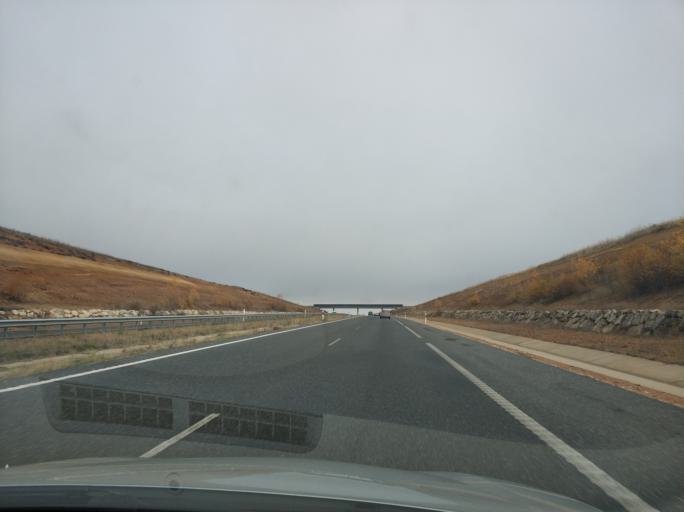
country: ES
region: Castille and Leon
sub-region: Provincia de Leon
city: Valdefresno
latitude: 42.5633
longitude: -5.5275
